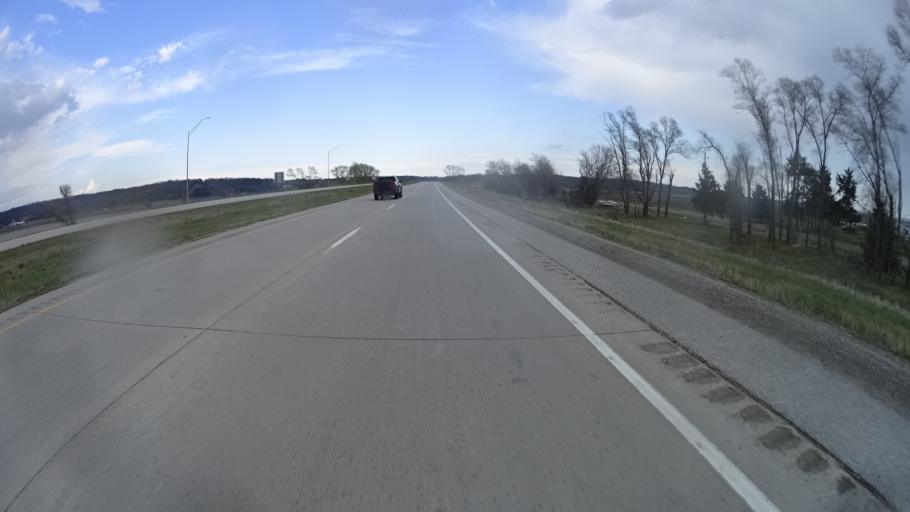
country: US
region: Iowa
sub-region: Mills County
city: Glenwood
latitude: 41.0457
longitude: -95.8137
